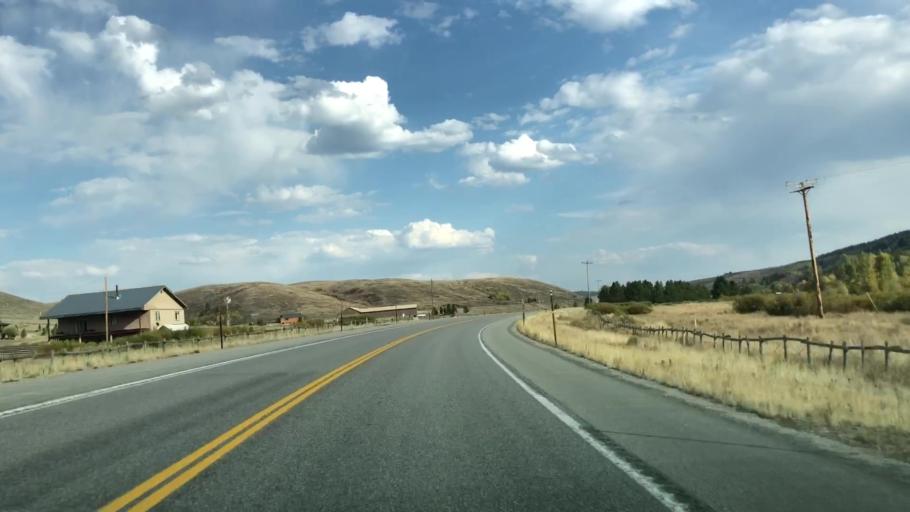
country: US
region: Wyoming
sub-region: Teton County
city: Hoback
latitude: 43.2440
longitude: -110.4551
